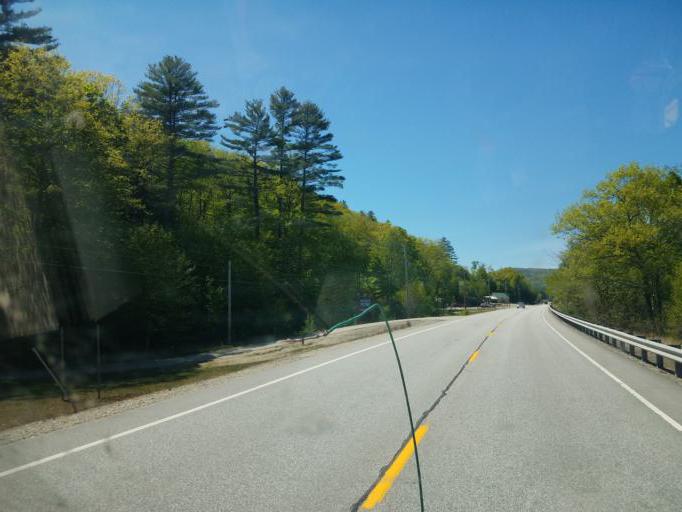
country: US
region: New Hampshire
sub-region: Grafton County
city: Rumney
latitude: 43.7842
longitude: -71.7855
